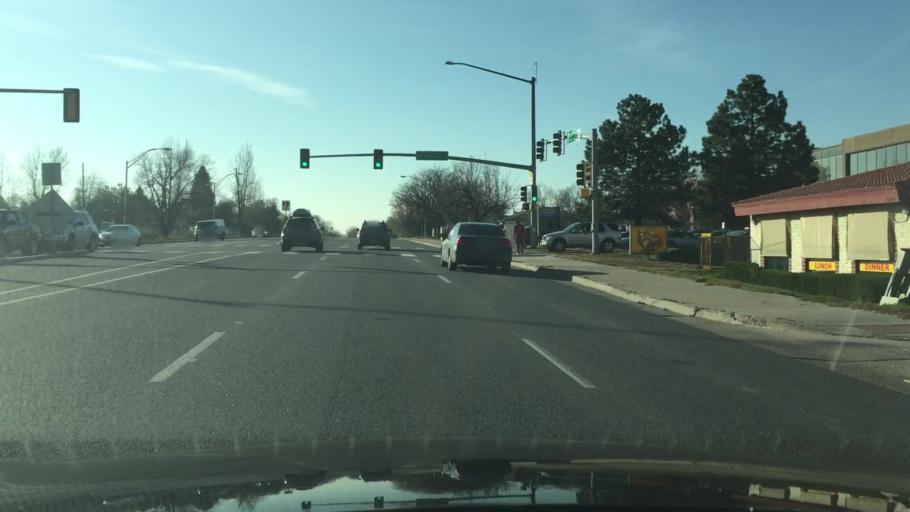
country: US
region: Colorado
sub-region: Arapahoe County
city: Dove Valley
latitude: 39.6532
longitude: -104.8126
